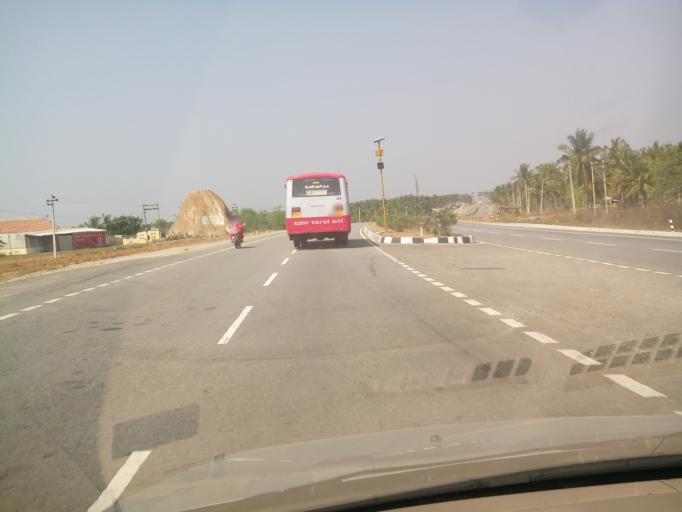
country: IN
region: Karnataka
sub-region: Hassan
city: Channarayapatna
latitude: 12.9101
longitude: 76.4463
